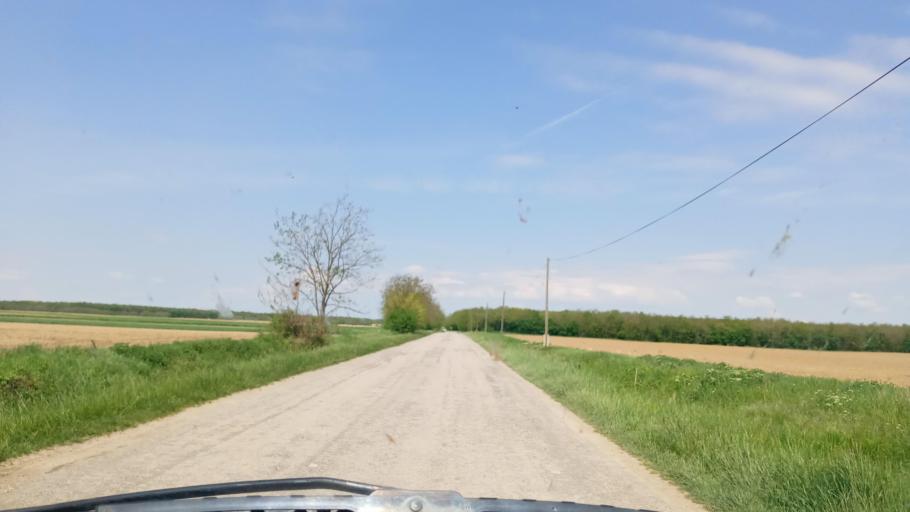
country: HU
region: Baranya
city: Boly
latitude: 45.8787
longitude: 18.5759
